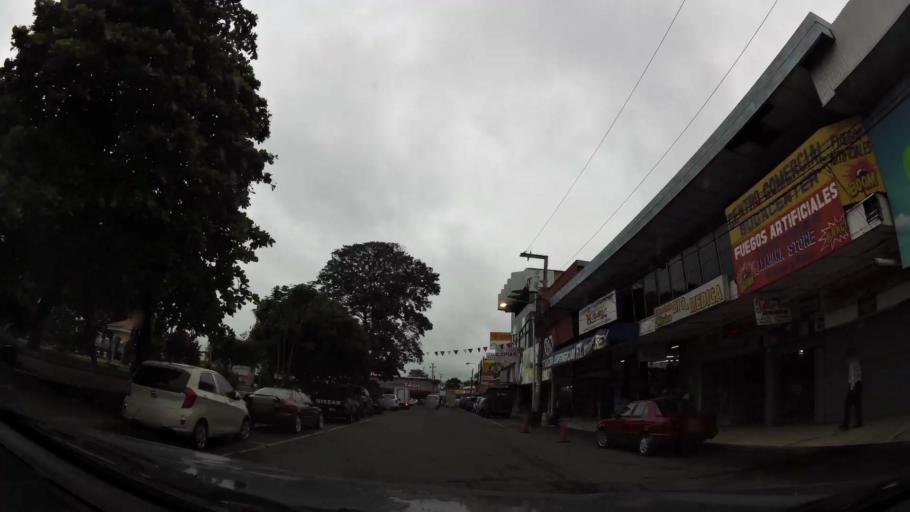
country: PA
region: Chiriqui
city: La Concepcion
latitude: 8.5179
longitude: -82.6196
